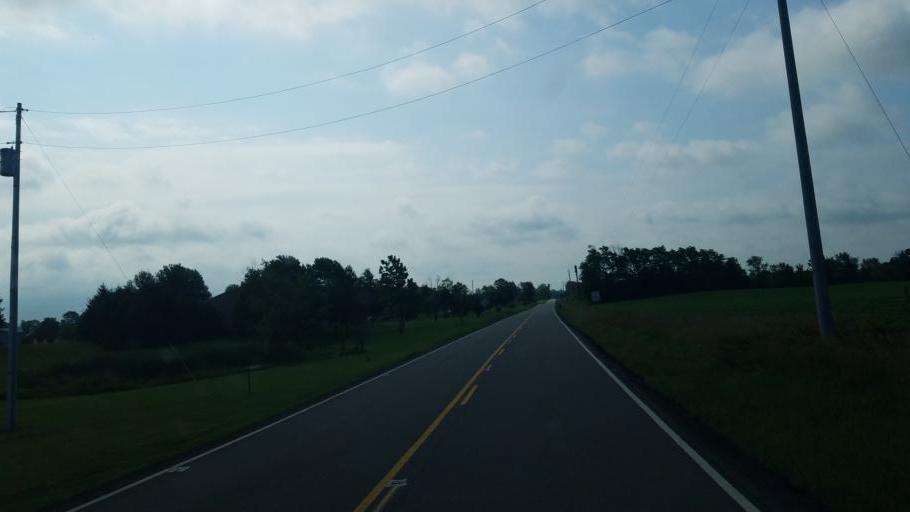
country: US
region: Ohio
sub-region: Knox County
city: Centerburg
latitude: 40.3171
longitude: -82.6613
